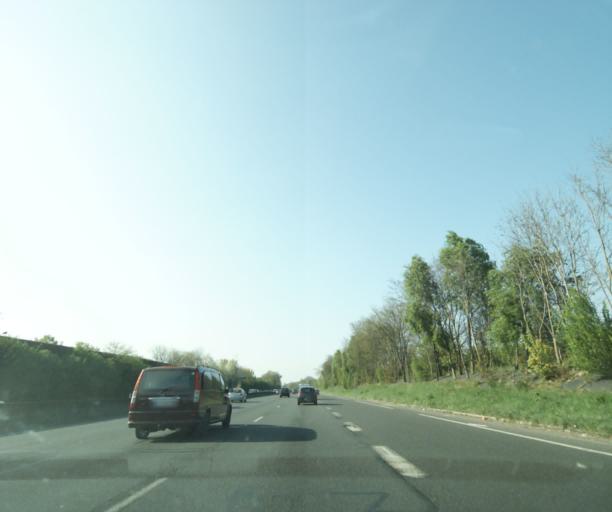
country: FR
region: Ile-de-France
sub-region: Departement de l'Essonne
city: Grigny
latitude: 48.6526
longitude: 2.3820
